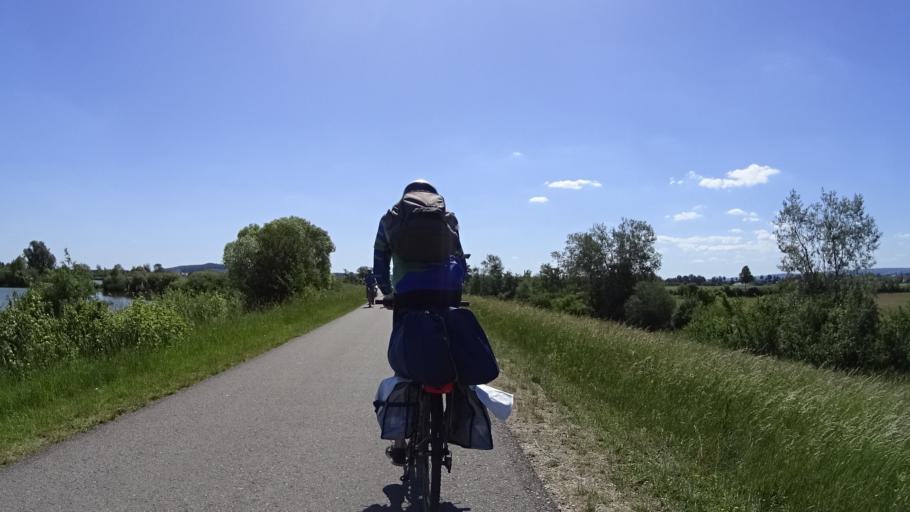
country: DE
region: Bavaria
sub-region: Regierungsbezirk Mittelfranken
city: Gunzenhausen
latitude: 49.1202
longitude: 10.7284
